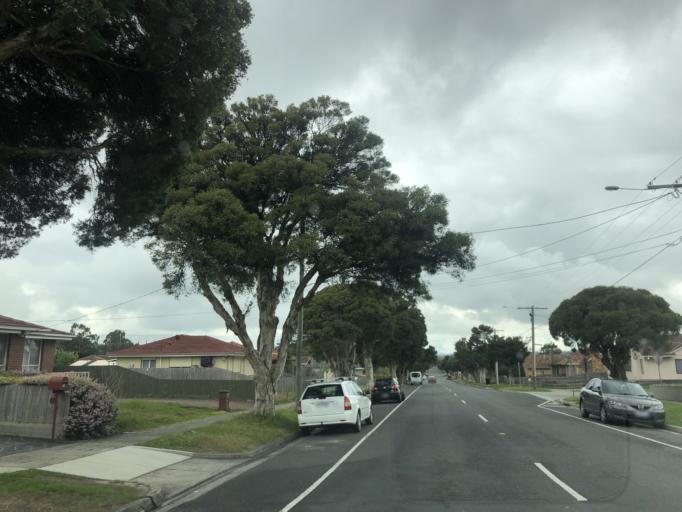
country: AU
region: Victoria
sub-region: Greater Dandenong
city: Dandenong North
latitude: -37.9638
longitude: 145.2133
